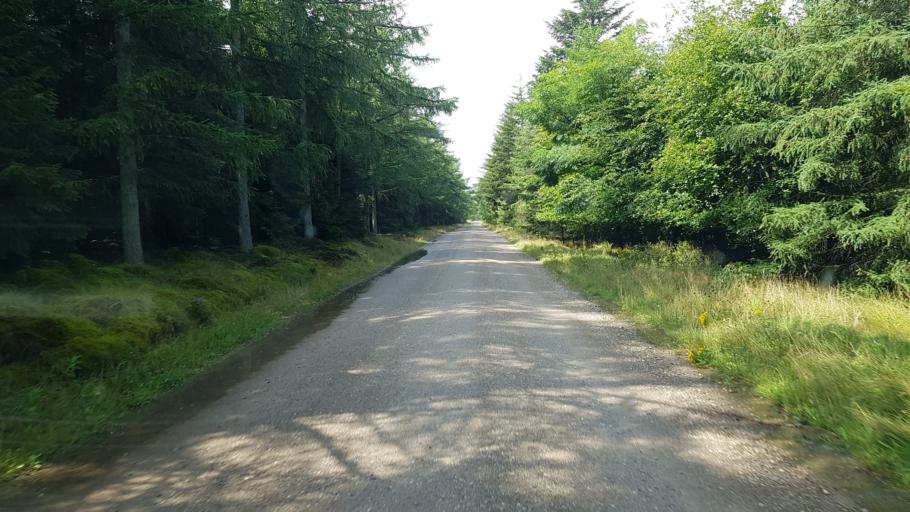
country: DK
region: South Denmark
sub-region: Vejen Kommune
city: Holsted
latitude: 55.5944
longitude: 8.9119
